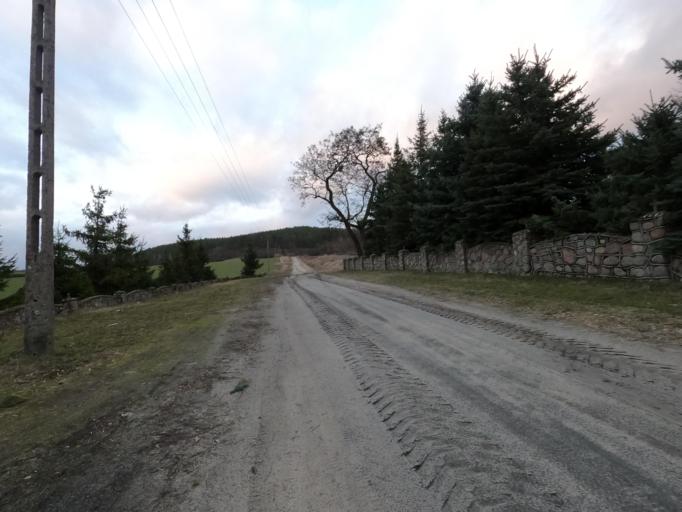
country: PL
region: Greater Poland Voivodeship
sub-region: Powiat pilski
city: Wyrzysk
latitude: 53.1136
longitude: 17.2031
